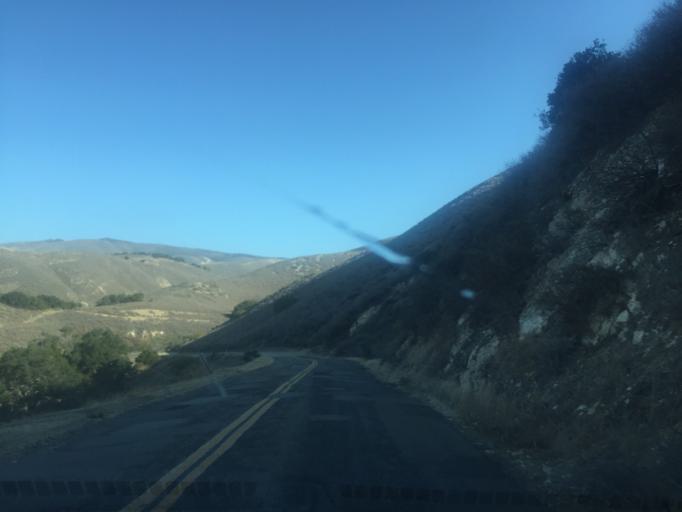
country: US
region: California
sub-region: Santa Barbara County
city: Lompoc
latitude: 34.5107
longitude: -120.4889
